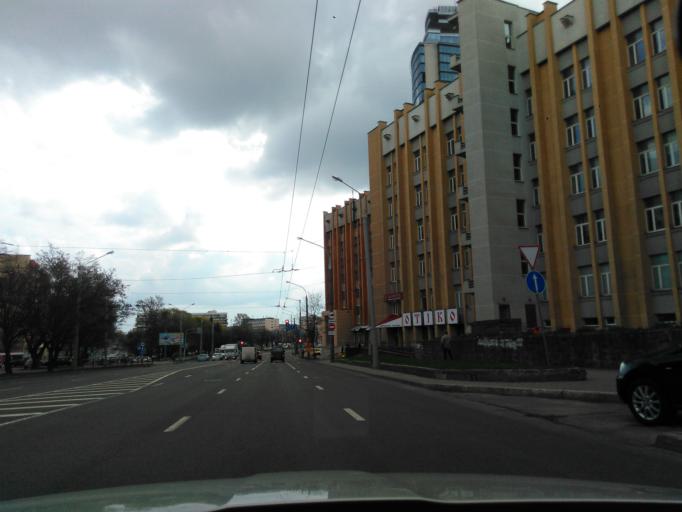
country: BY
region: Minsk
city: Minsk
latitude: 53.9083
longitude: 27.5306
